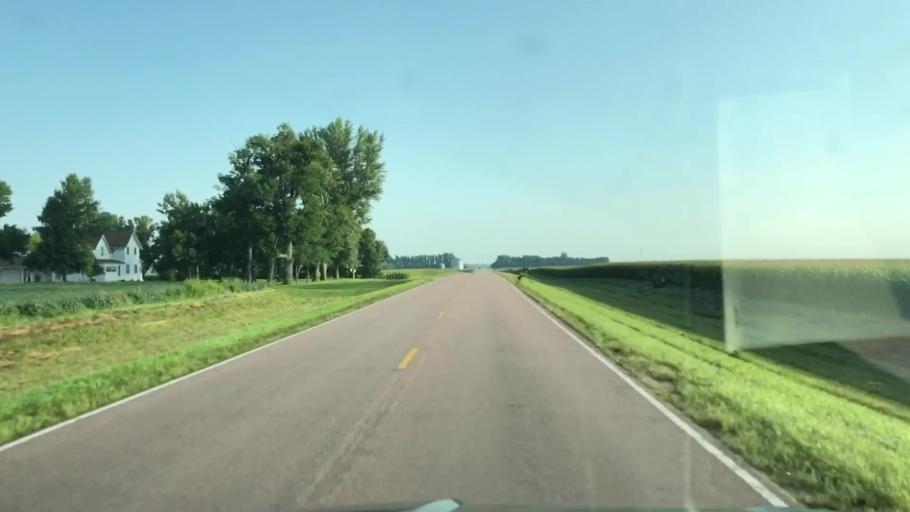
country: US
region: Iowa
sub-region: Lyon County
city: George
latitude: 43.3108
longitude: -95.9991
